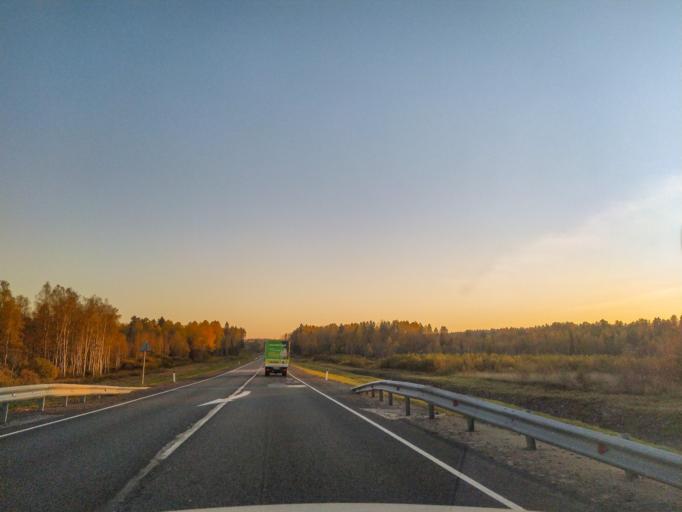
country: RU
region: Leningrad
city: Kuznechnoye
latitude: 61.2646
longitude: 29.7529
